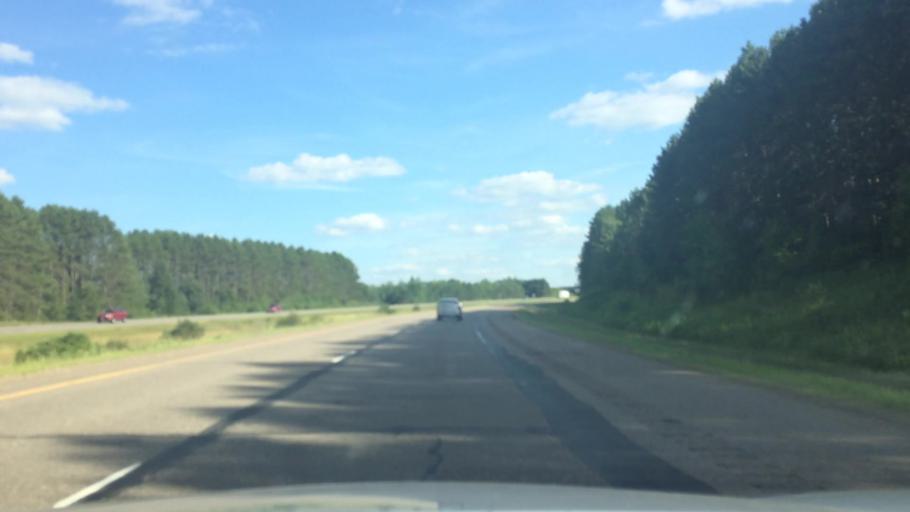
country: US
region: Wisconsin
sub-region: Lincoln County
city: Merrill
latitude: 45.1972
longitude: -89.6492
